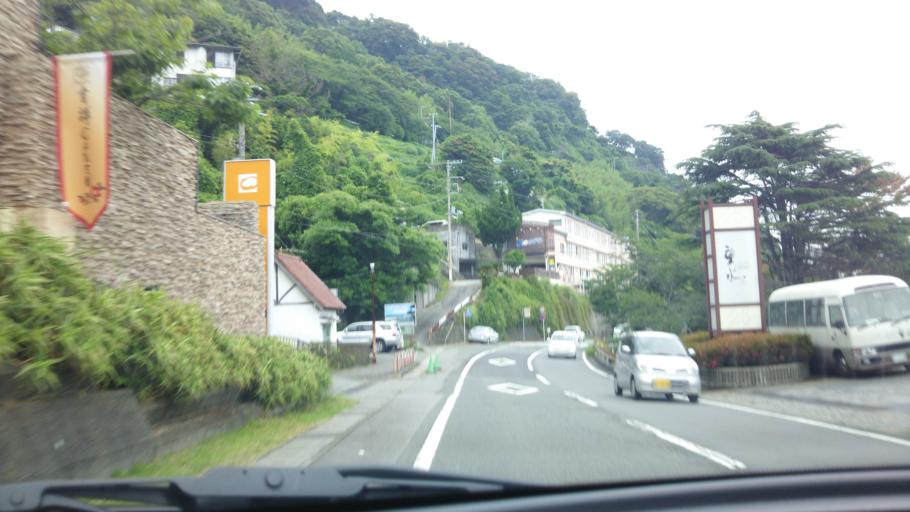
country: JP
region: Shizuoka
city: Ito
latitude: 34.8316
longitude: 139.0747
